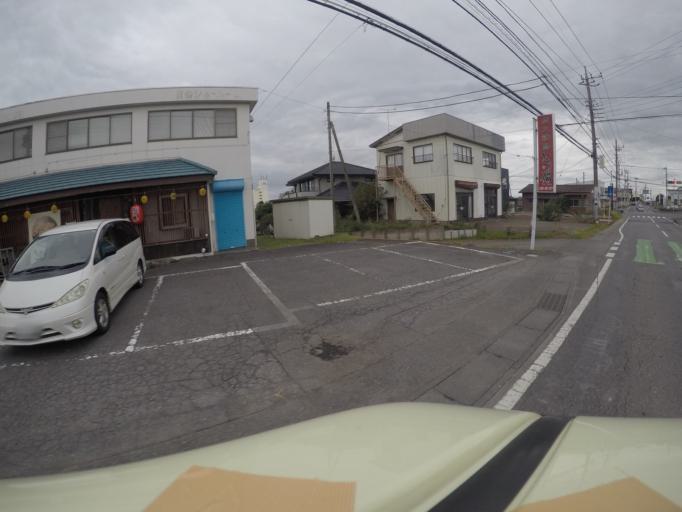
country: JP
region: Ibaraki
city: Naka
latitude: 36.0865
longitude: 140.1292
